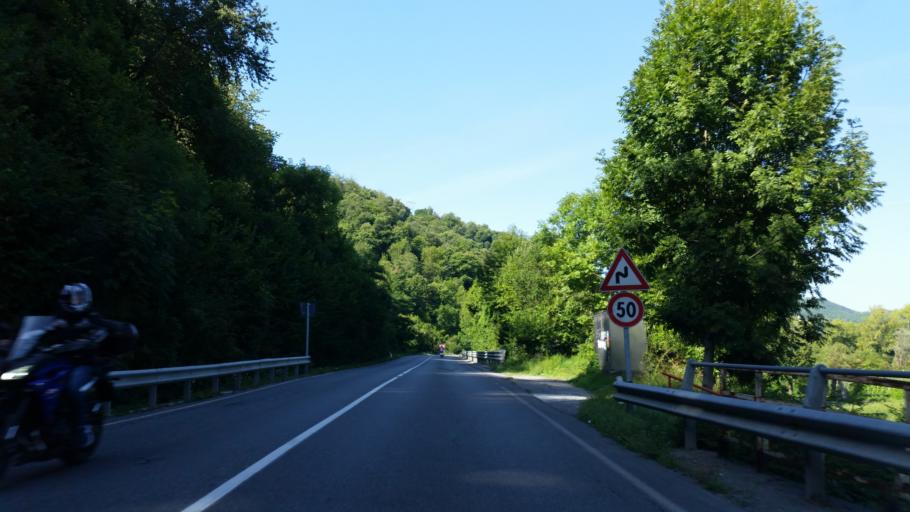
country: IT
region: Piedmont
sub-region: Provincia di Cuneo
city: Borgo San Dalmazzo
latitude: 44.3283
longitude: 7.5118
